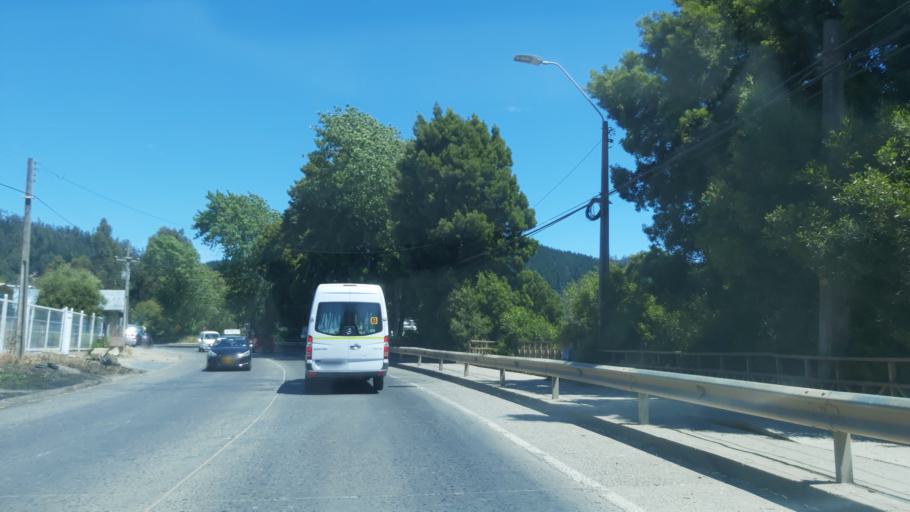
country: CL
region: Maule
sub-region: Provincia de Talca
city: Constitucion
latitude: -35.3391
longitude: -72.4205
